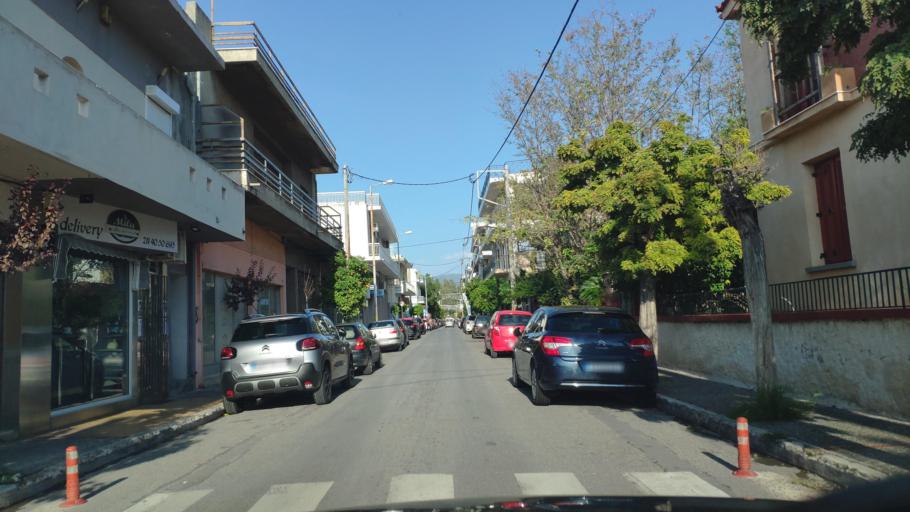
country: GR
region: Attica
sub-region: Nomarchia Dytikis Attikis
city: Elefsina
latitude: 38.0407
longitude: 23.5404
